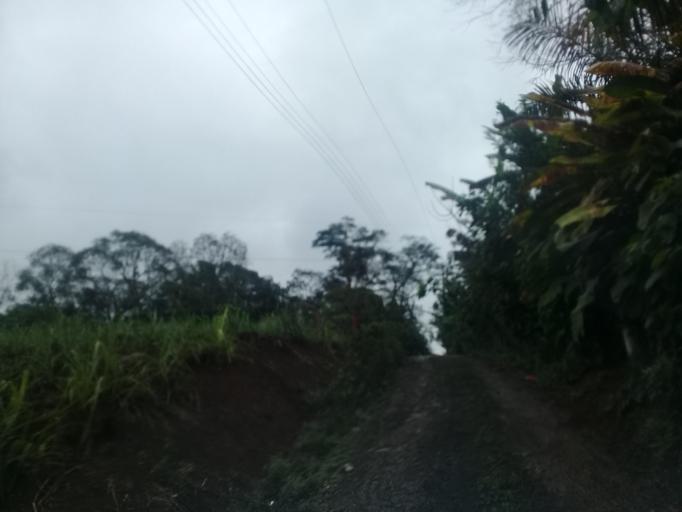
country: MX
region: Veracruz
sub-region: Amatlan de los Reyes
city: Centro de Readaptacion Social
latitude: 18.8226
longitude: -96.9558
